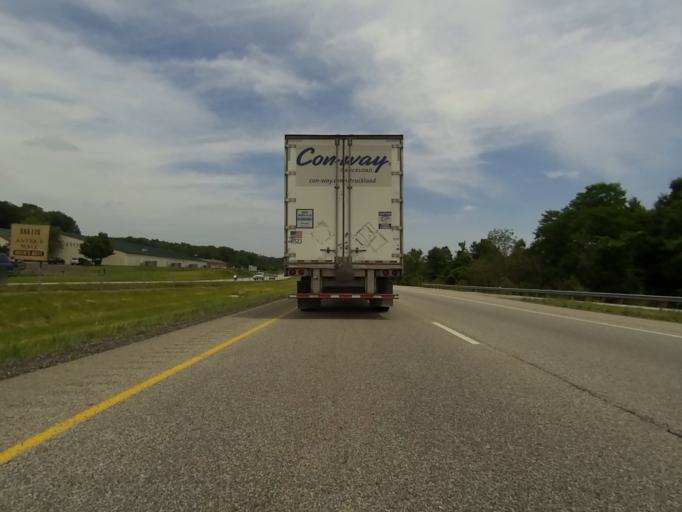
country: US
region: Ohio
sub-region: Portage County
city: Ravenna
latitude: 41.1093
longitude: -81.2385
